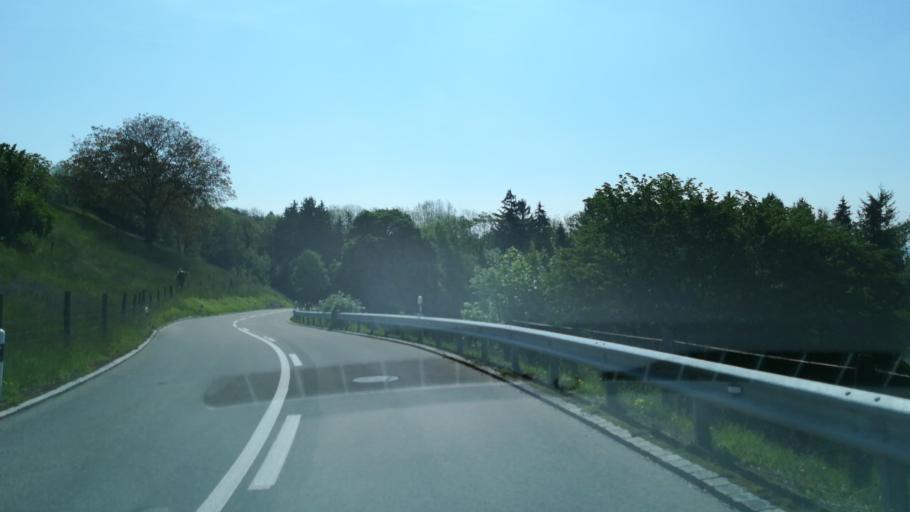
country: CH
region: Thurgau
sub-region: Weinfelden District
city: Wigoltingen
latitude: 47.6235
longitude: 9.0384
